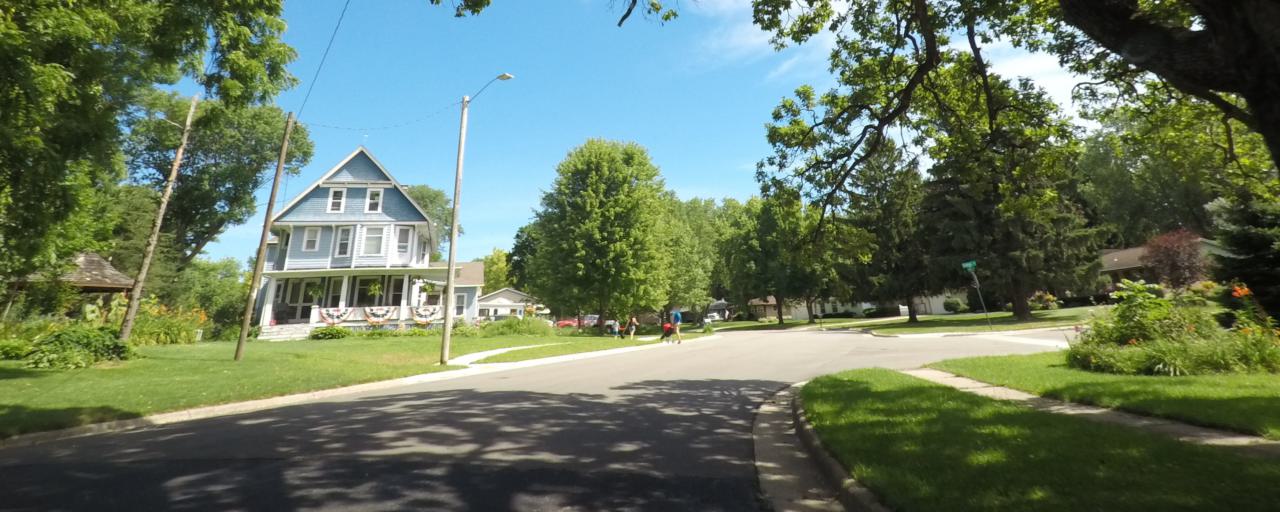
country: US
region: Wisconsin
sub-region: Dane County
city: McFarland
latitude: 43.0185
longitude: -89.2886
